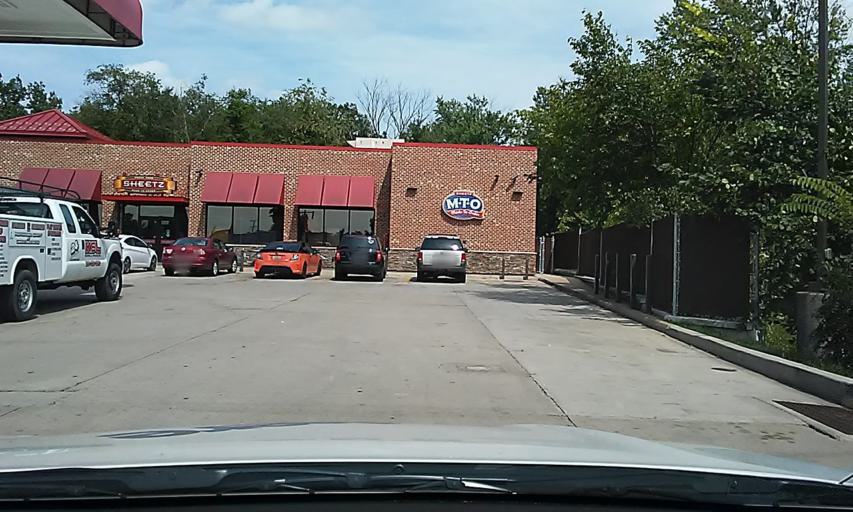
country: US
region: Pennsylvania
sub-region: Westmoreland County
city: Latrobe
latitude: 40.3981
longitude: -79.4216
